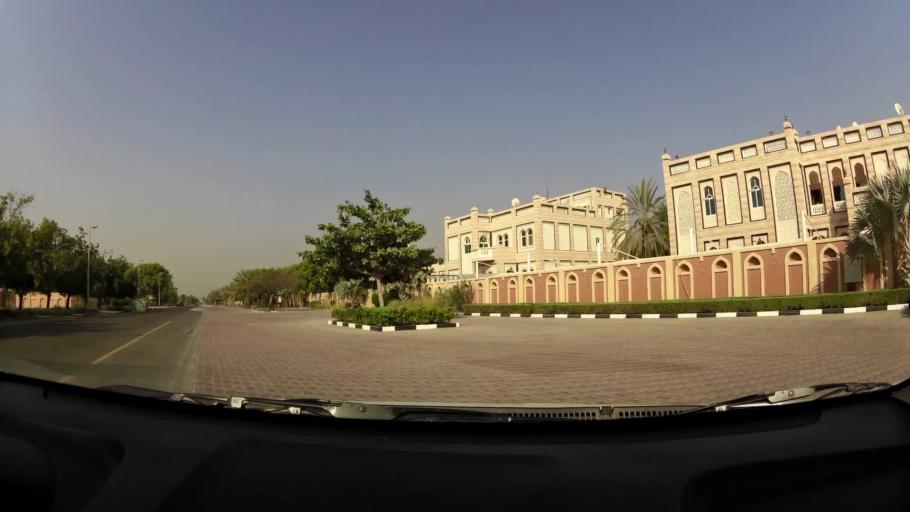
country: AE
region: Ash Shariqah
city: Sharjah
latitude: 25.3139
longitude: 55.3441
